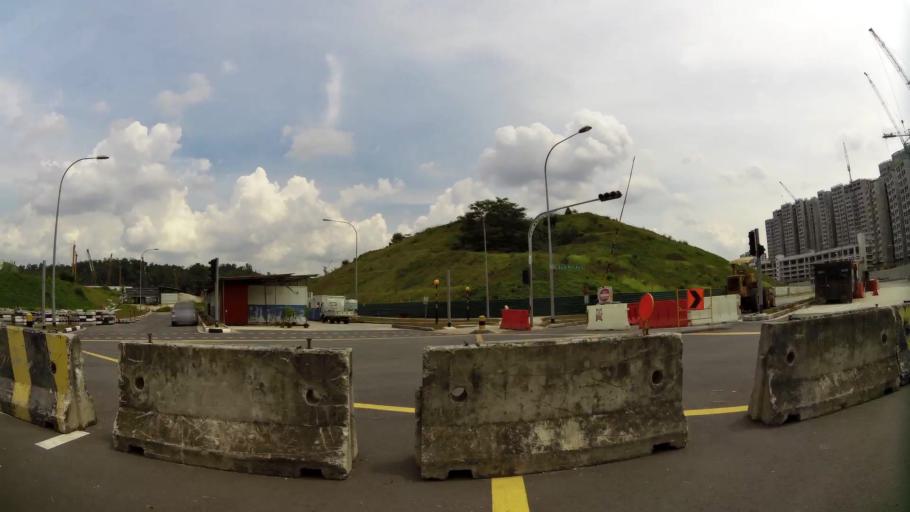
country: MY
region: Johor
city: Johor Bahru
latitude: 1.3544
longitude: 103.7417
